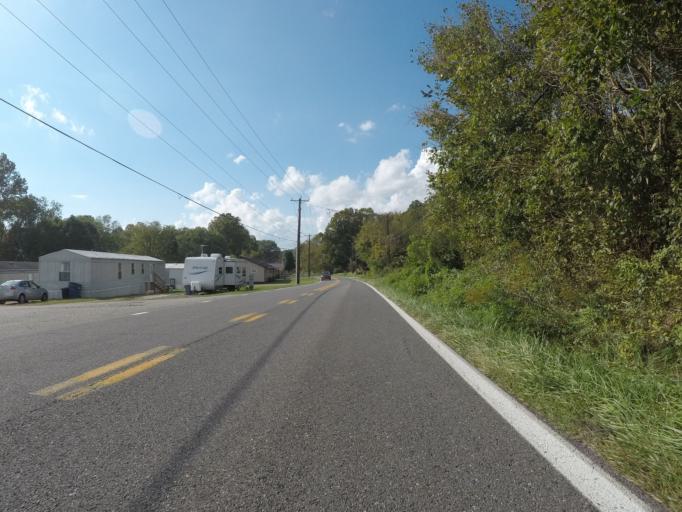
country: US
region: West Virginia
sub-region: Wayne County
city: Lavalette
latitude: 38.3522
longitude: -82.5002
